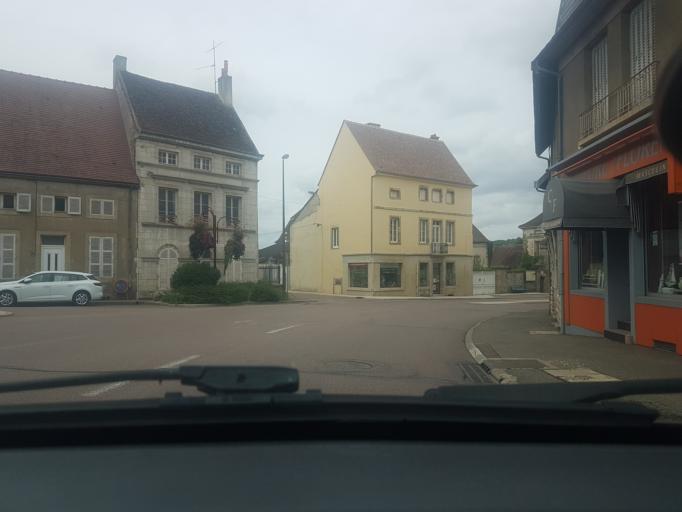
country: FR
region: Bourgogne
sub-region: Departement de la Cote-d'Or
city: Arnay-le-Duc
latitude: 47.1339
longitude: 4.4860
